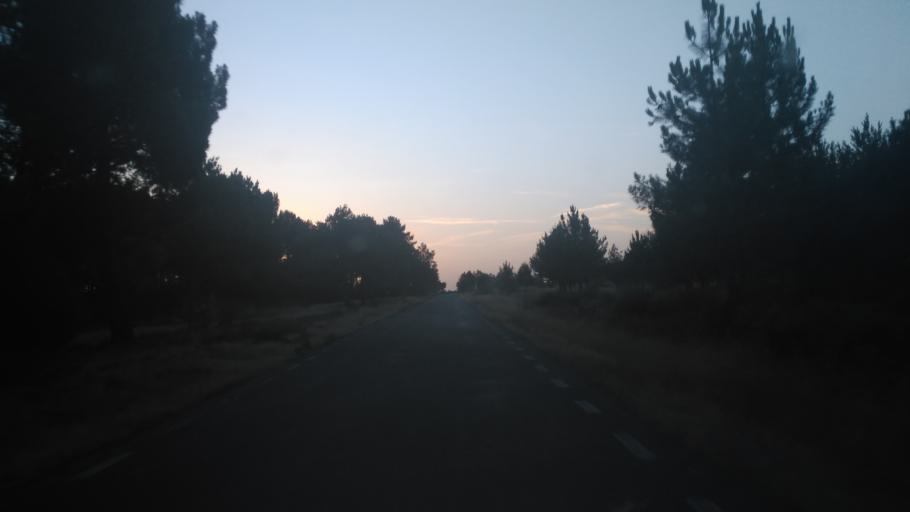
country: ES
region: Castille and Leon
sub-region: Provincia de Salamanca
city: Nava de Francia
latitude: 40.5235
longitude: -6.1145
